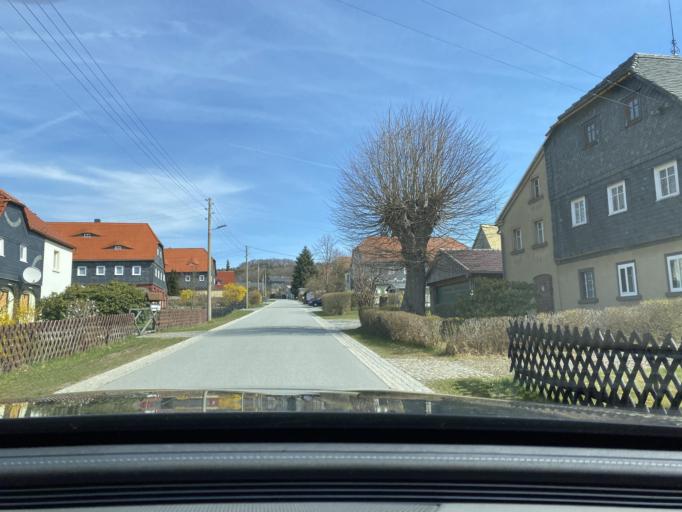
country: DE
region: Saxony
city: Eibau
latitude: 50.9992
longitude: 14.6451
